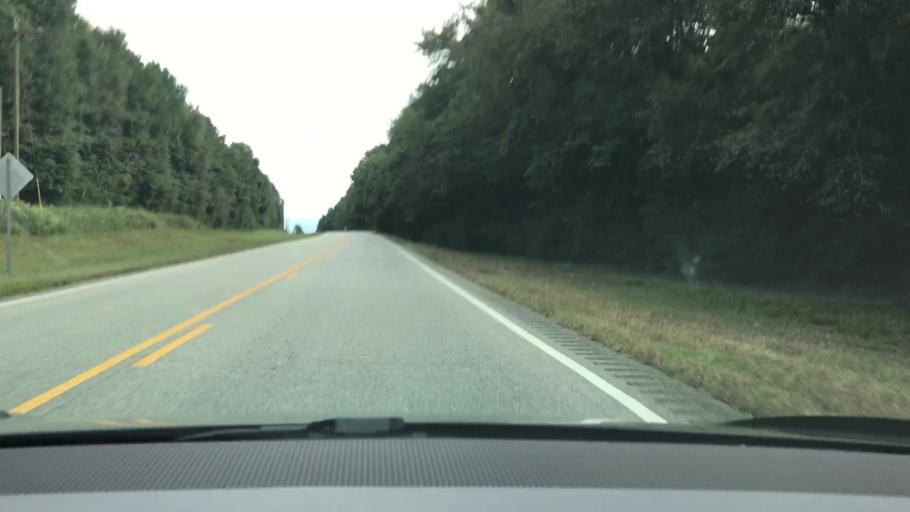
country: US
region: Alabama
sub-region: Pike County
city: Troy
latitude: 31.6423
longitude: -85.9711
